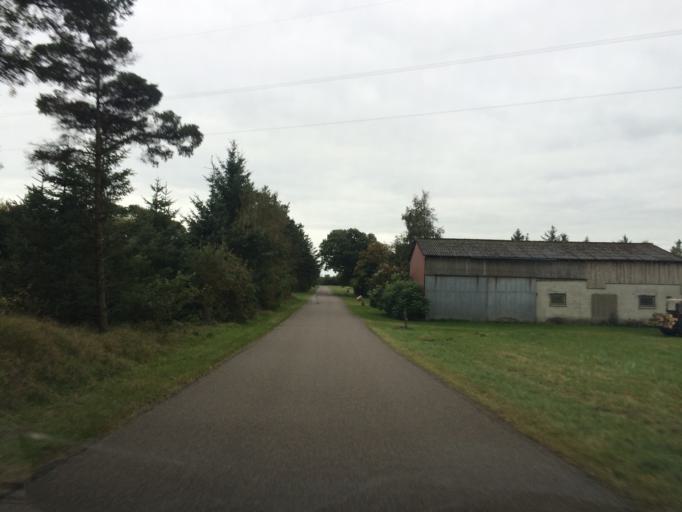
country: DK
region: Central Jutland
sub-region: Holstebro Kommune
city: Ulfborg
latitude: 56.2303
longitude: 8.4371
